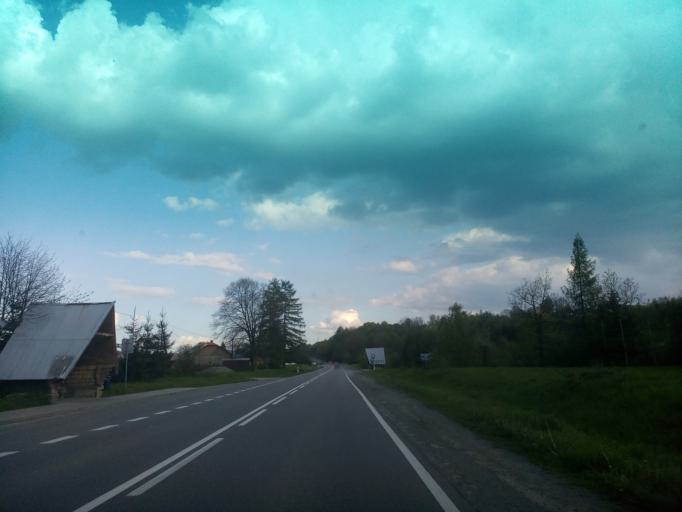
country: PL
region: Lesser Poland Voivodeship
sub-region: Powiat nowosadecki
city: Kamionka Wielka
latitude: 49.5371
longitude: 20.8131
